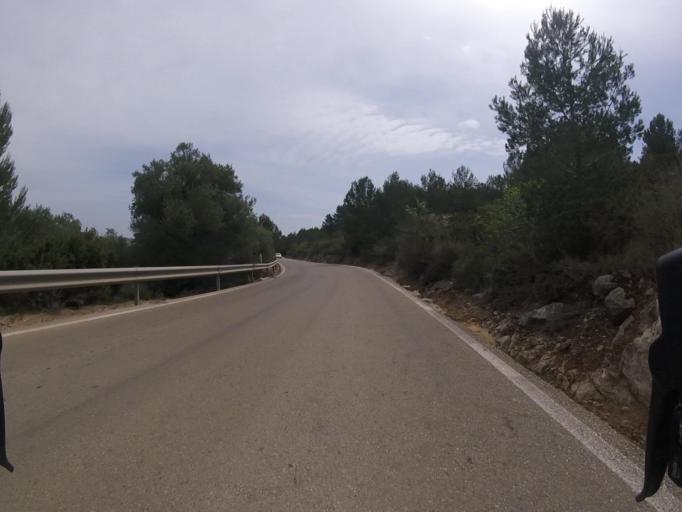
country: ES
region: Valencia
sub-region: Provincia de Castello
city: Cabanes
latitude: 40.1598
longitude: 0.0786
